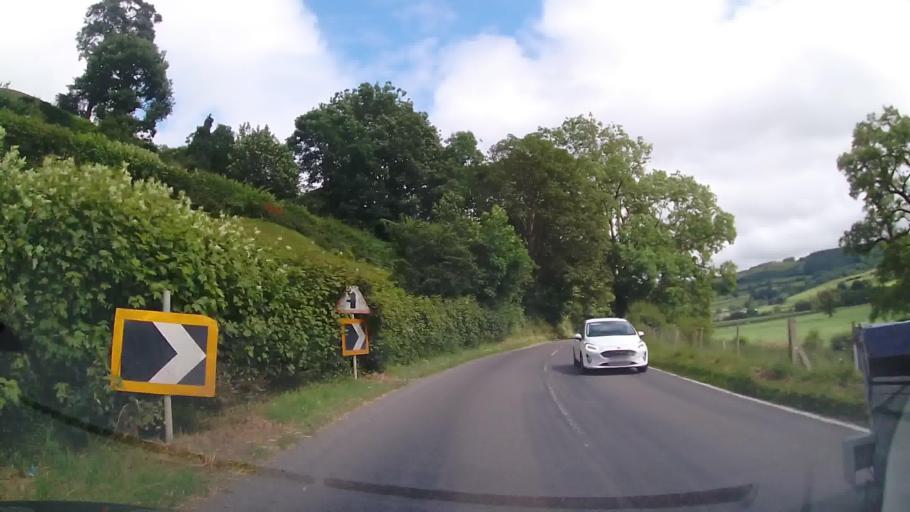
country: GB
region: Wales
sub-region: Sir Powys
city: Llanfechain
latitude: 52.8120
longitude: -3.2354
